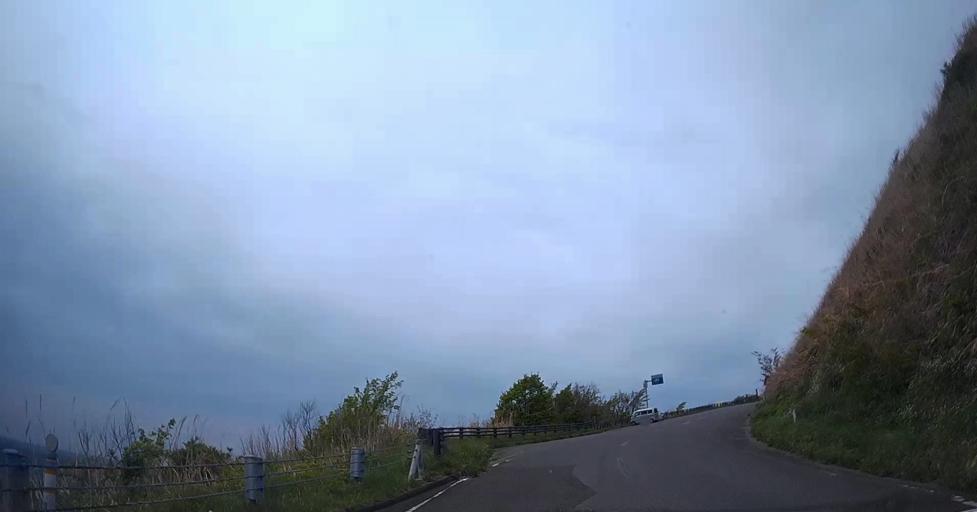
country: JP
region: Aomori
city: Shimokizukuri
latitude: 41.1952
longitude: 140.3355
